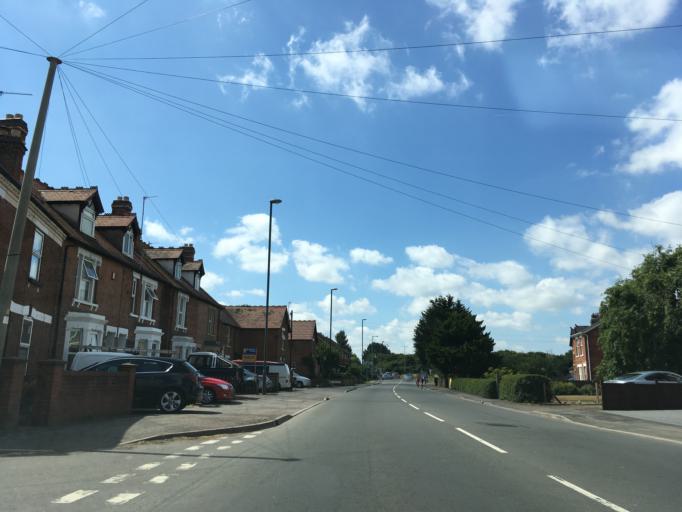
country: GB
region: England
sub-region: Gloucestershire
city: Gloucester
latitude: 51.8846
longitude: -2.2367
